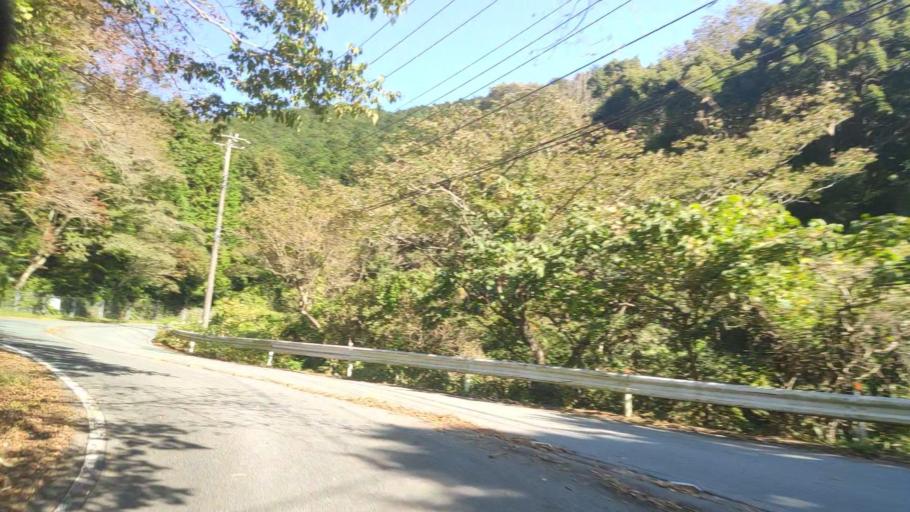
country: JP
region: Shizuoka
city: Atami
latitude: 35.0504
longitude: 139.0439
